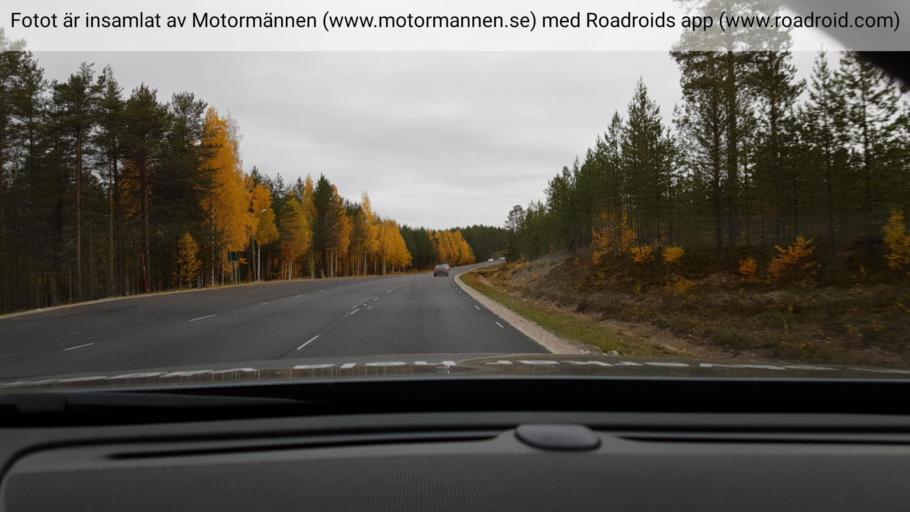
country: SE
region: Norrbotten
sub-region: Overkalix Kommun
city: OEverkalix
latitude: 66.4424
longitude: 22.7873
